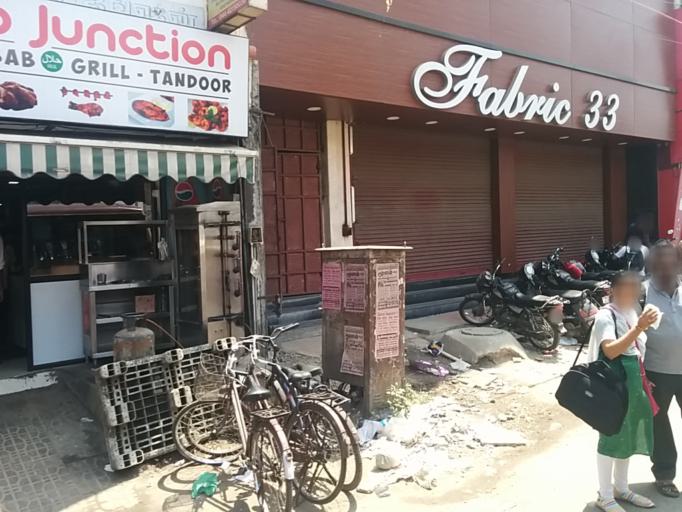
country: IN
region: Tamil Nadu
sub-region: Chennai
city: Chetput
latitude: 13.0594
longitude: 80.2656
